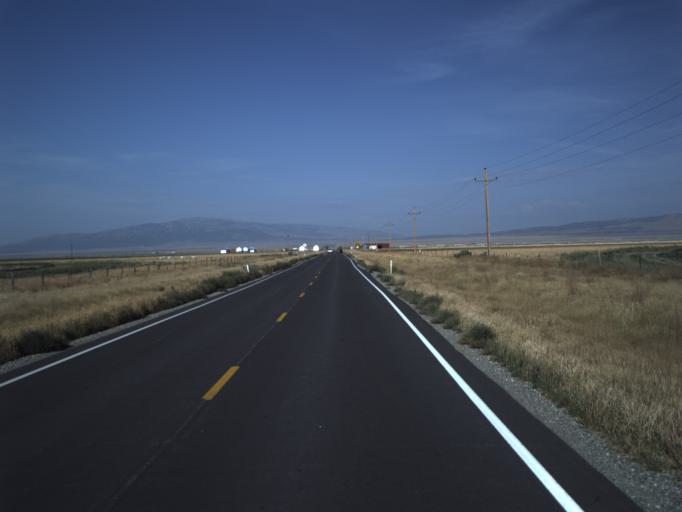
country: US
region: Idaho
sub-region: Oneida County
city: Malad City
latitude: 41.9671
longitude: -112.8578
